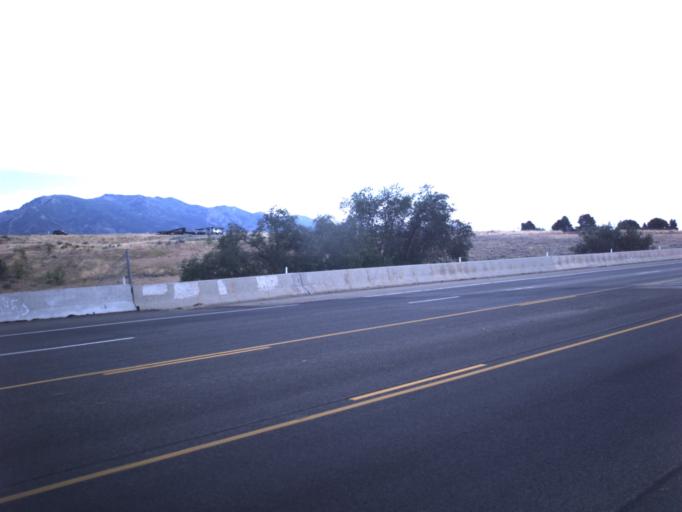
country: US
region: Utah
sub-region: Weber County
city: West Haven
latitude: 41.2011
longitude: -112.0259
